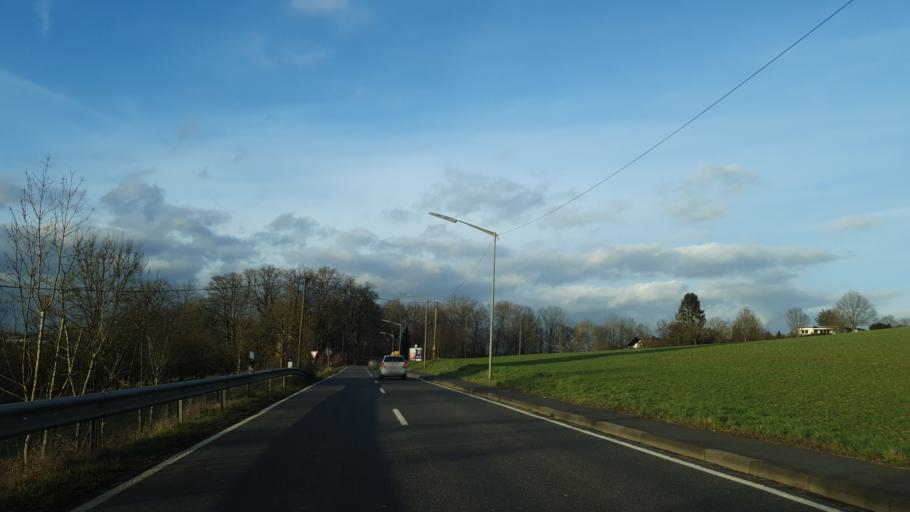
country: DE
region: Rheinland-Pfalz
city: Almersbach
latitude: 50.6798
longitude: 7.6374
